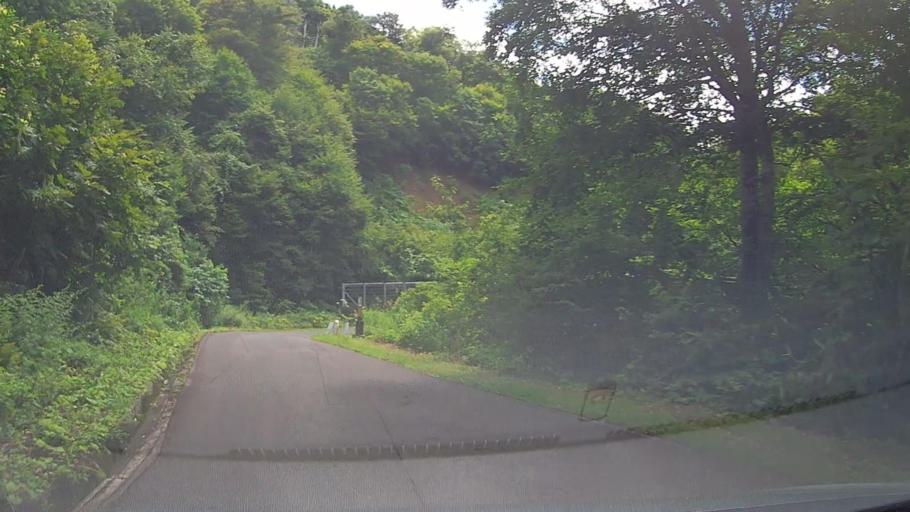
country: JP
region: Nagano
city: Iiyama
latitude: 36.9274
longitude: 138.4698
